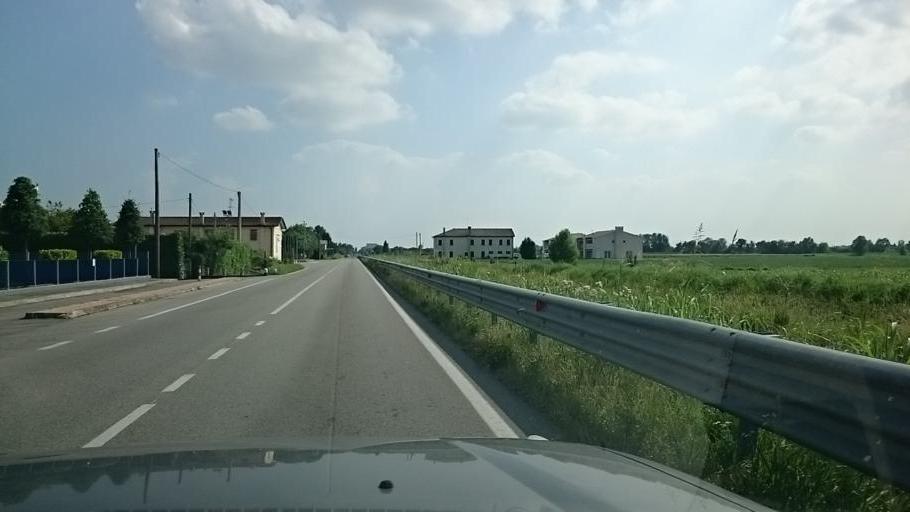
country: IT
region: Veneto
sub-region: Provincia di Padova
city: Cavino
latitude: 45.5319
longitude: 11.8710
